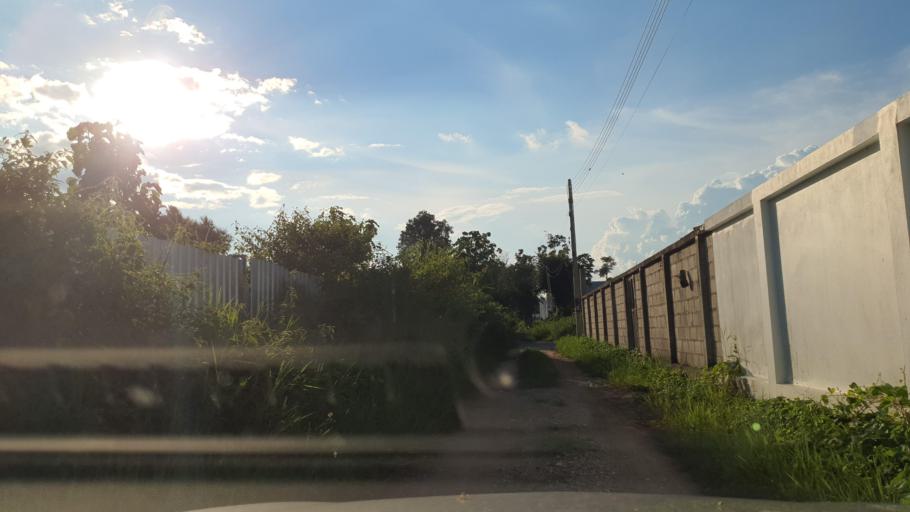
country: TH
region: Chiang Mai
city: Hang Dong
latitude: 18.6818
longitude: 98.8861
